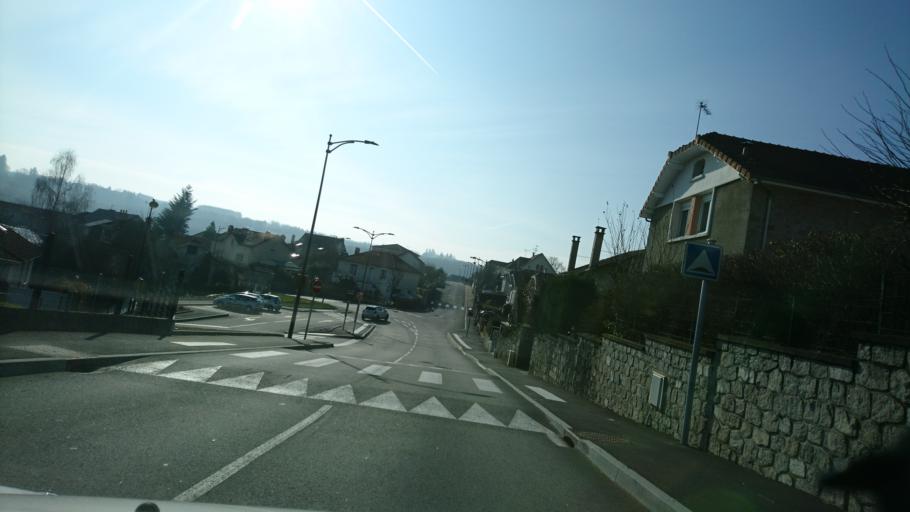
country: FR
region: Limousin
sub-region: Departement de la Haute-Vienne
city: Le Palais-sur-Vienne
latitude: 45.8655
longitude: 1.3221
